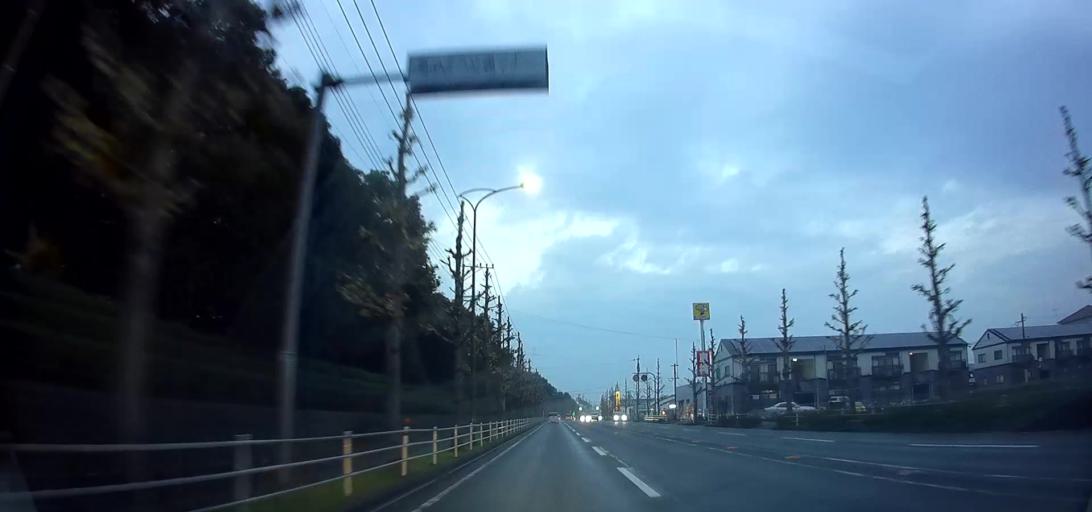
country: JP
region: Nagasaki
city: Omura
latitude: 32.9162
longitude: 129.9439
